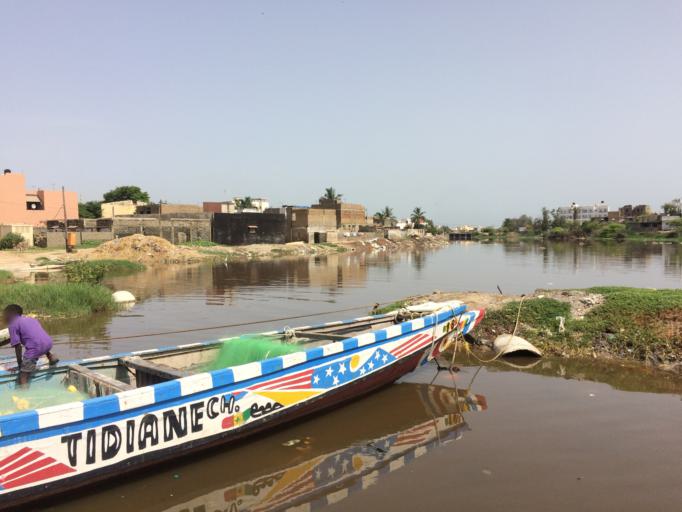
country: SN
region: Dakar
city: Pikine
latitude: 14.7298
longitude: -17.3259
